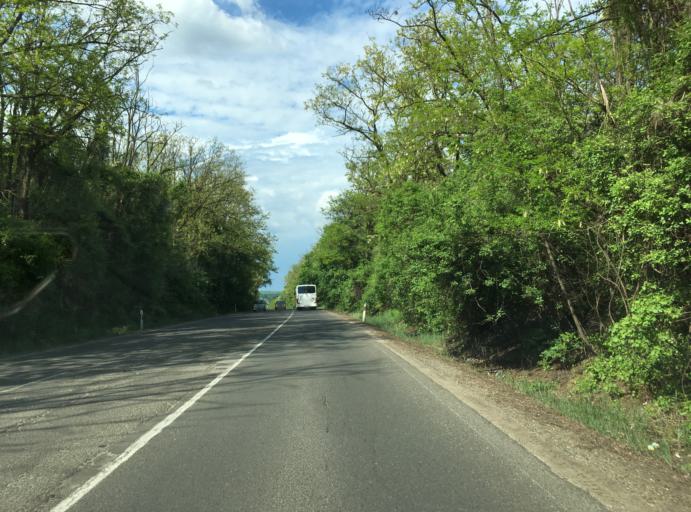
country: HU
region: Pest
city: Bag
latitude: 47.6370
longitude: 19.4616
